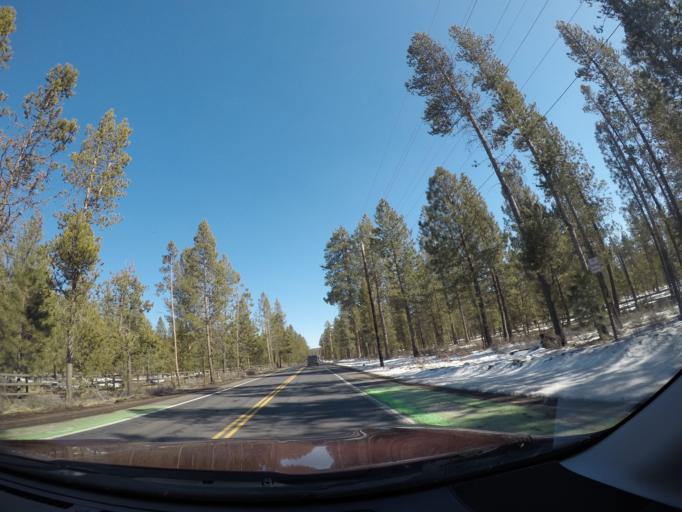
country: US
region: Oregon
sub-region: Deschutes County
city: Sunriver
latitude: 43.8633
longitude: -121.4471
